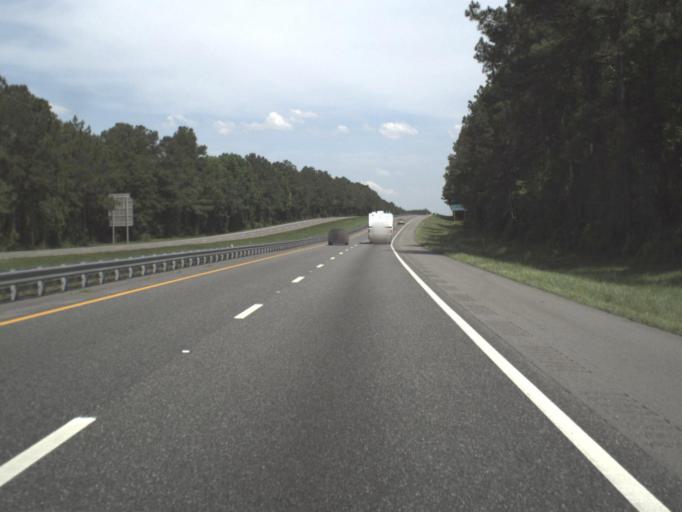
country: US
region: Florida
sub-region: Suwannee County
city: Wellborn
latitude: 30.2629
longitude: -82.7377
